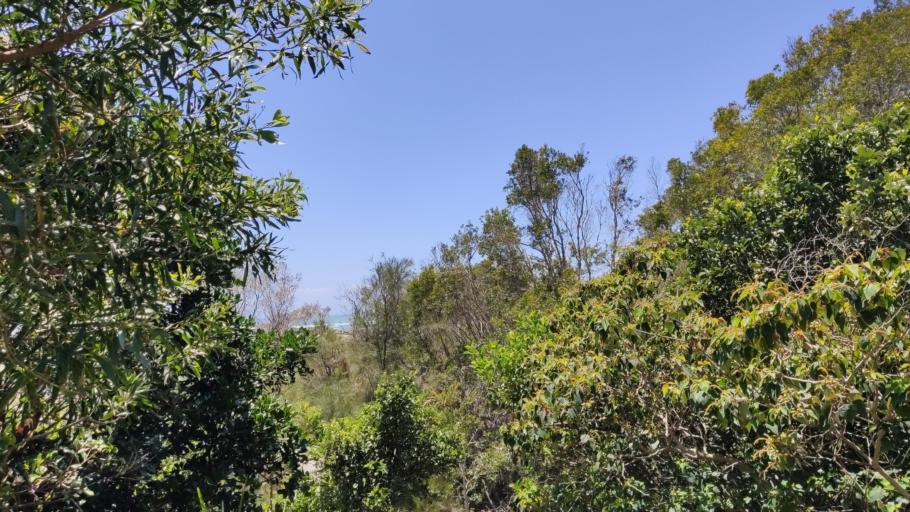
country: AU
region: New South Wales
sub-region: Port Macquarie-Hastings
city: North Haven
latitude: -31.6397
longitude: 152.8363
